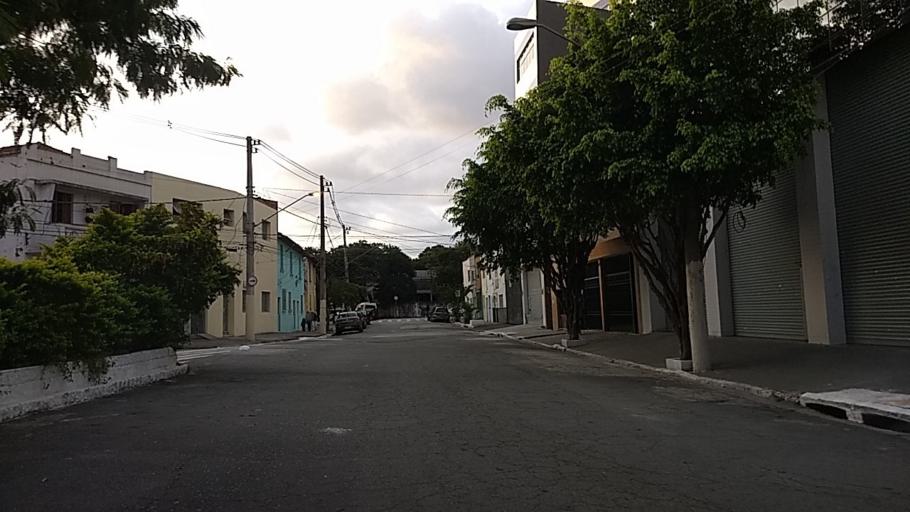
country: BR
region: Sao Paulo
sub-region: Sao Paulo
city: Sao Paulo
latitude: -23.5277
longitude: -46.6211
